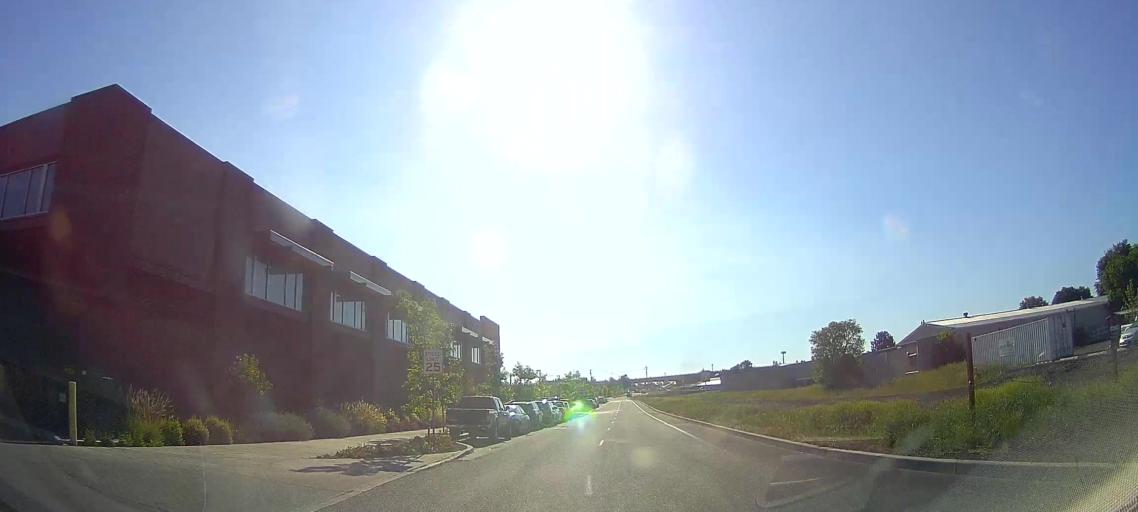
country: US
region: Oregon
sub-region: Deschutes County
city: Bend
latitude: 44.0517
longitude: -121.3138
